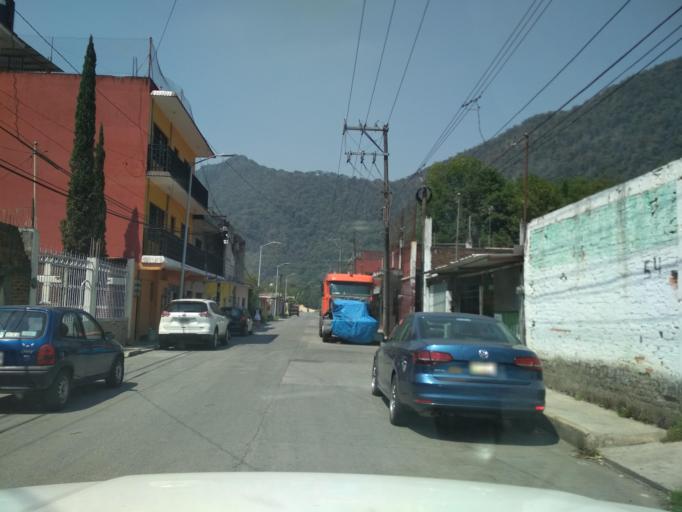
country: MX
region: Veracruz
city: Rio Blanco
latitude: 18.8428
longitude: -97.1223
